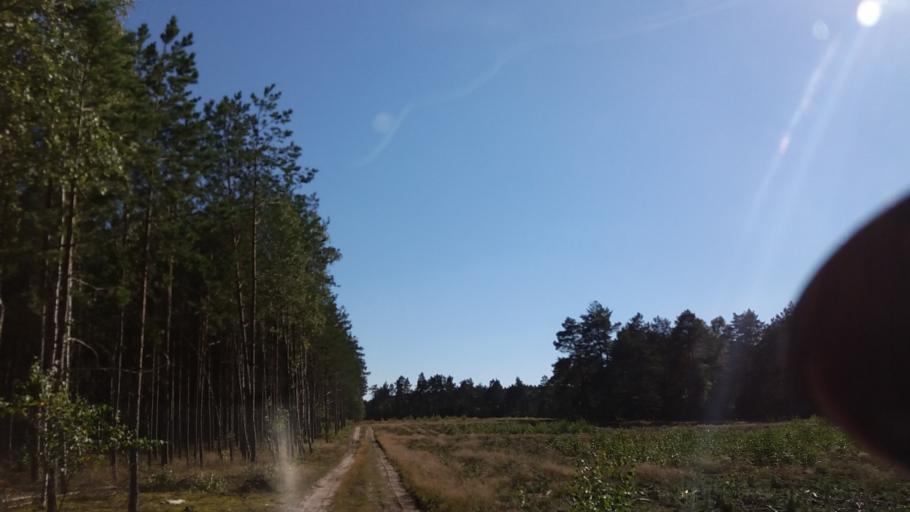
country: PL
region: West Pomeranian Voivodeship
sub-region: Powiat szczecinecki
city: Borne Sulinowo
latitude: 53.5745
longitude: 16.4873
